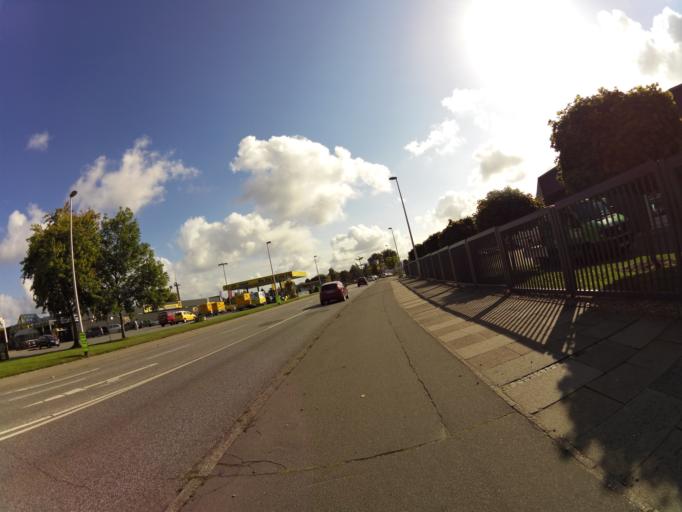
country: DE
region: Schleswig-Holstein
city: Eckernforde
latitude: 54.4509
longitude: 9.8315
